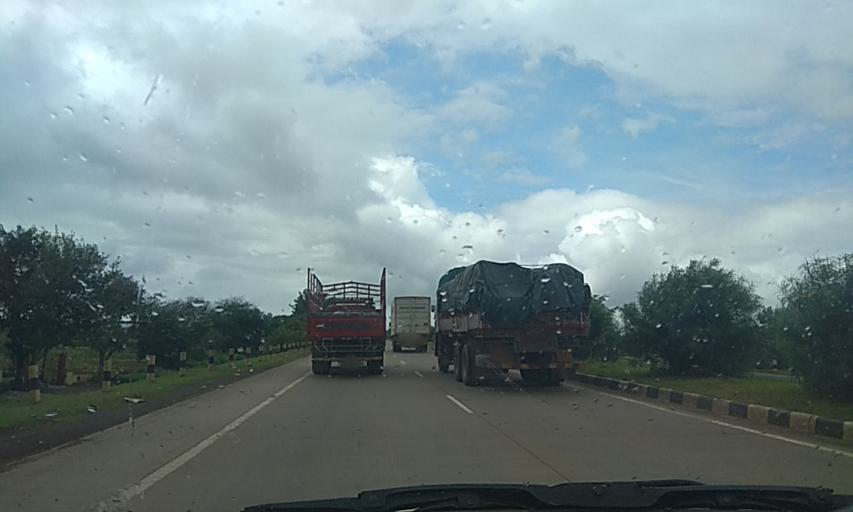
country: IN
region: Karnataka
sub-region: Belgaum
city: Sankeshwar
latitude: 16.3026
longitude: 74.4338
